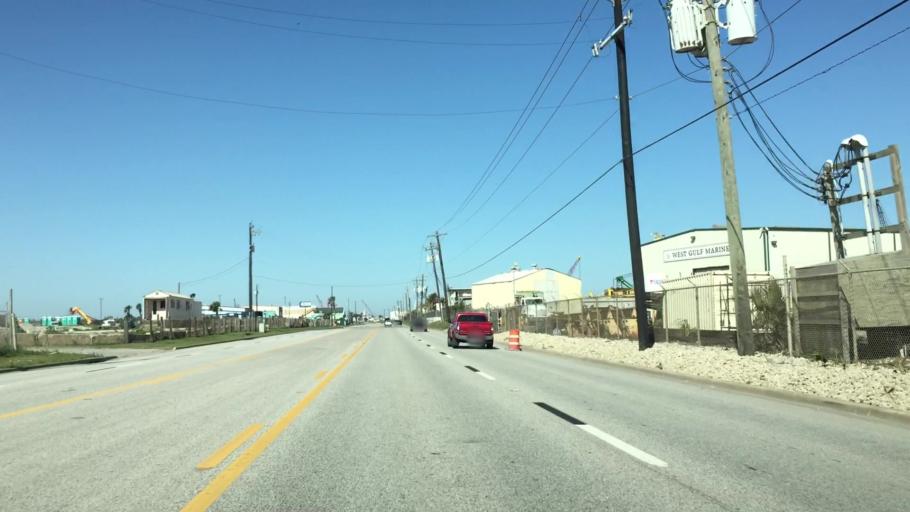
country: US
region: Texas
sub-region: Galveston County
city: Galveston
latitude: 29.2971
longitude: -94.8423
